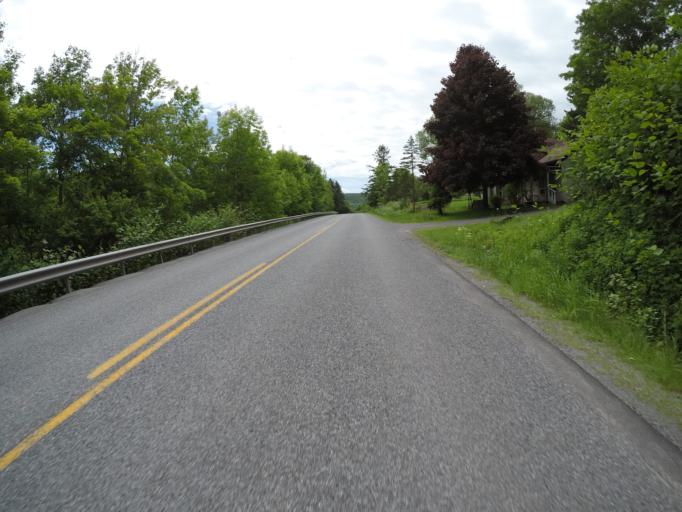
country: US
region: New York
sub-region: Delaware County
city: Stamford
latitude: 42.1982
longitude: -74.5782
